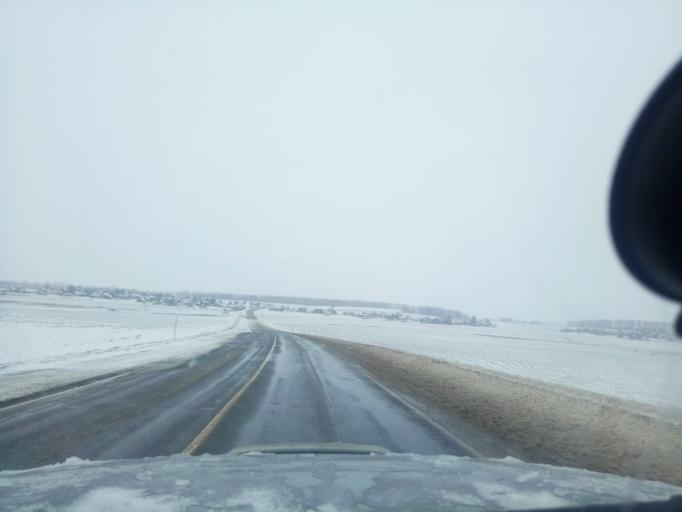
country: BY
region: Minsk
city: Haradzyeya
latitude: 53.3326
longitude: 26.5294
